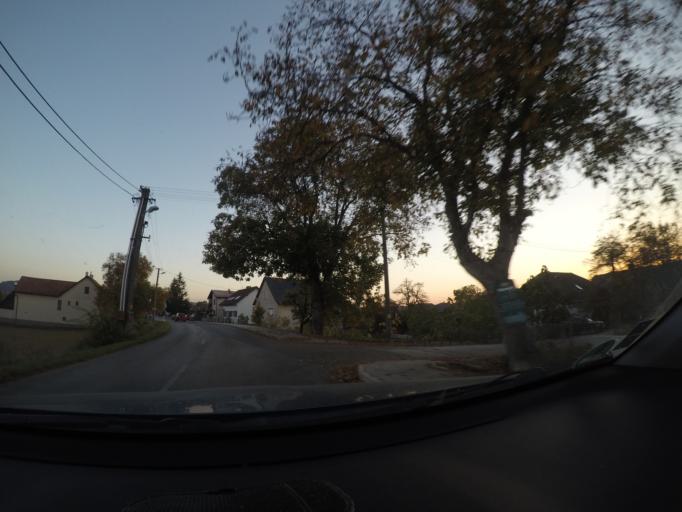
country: SK
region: Nitriansky
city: Nemsova
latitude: 48.9515
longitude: 18.0915
